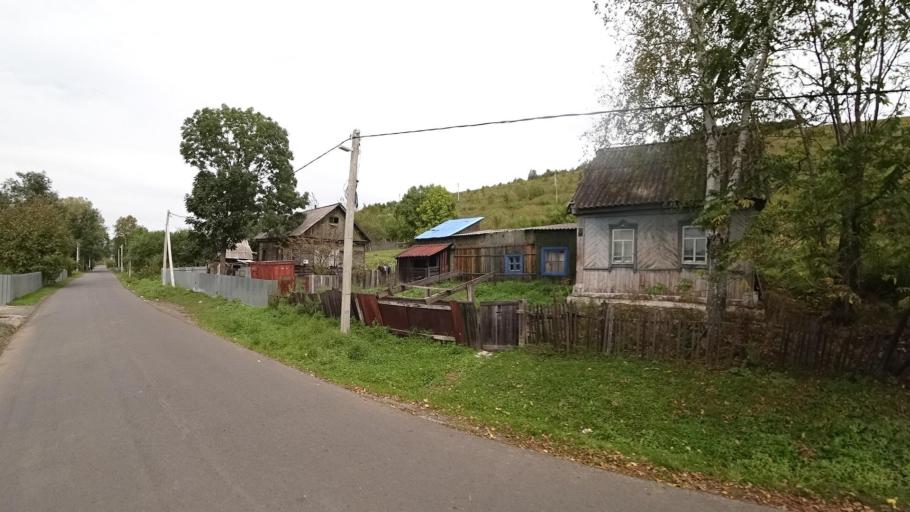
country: RU
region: Jewish Autonomous Oblast
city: Khingansk
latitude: 49.0267
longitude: 131.0589
